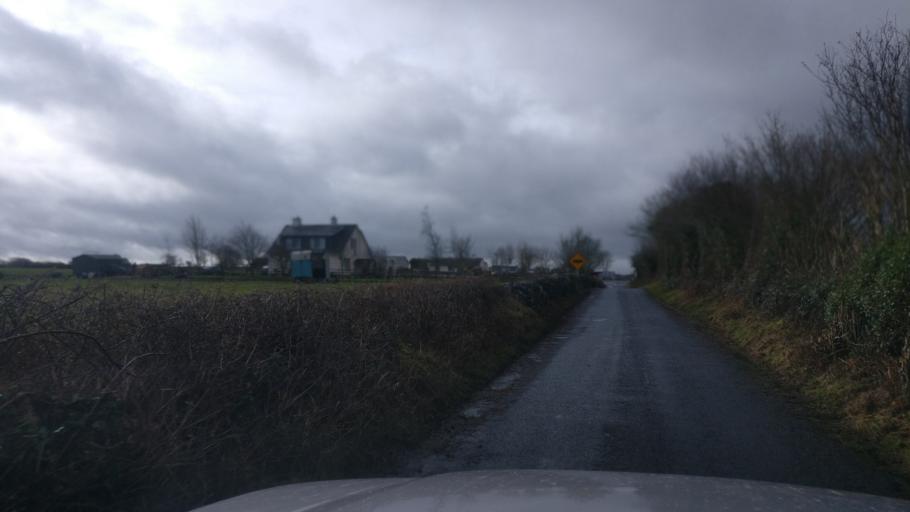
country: IE
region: Connaught
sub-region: County Galway
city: Athenry
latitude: 53.2584
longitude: -8.8031
